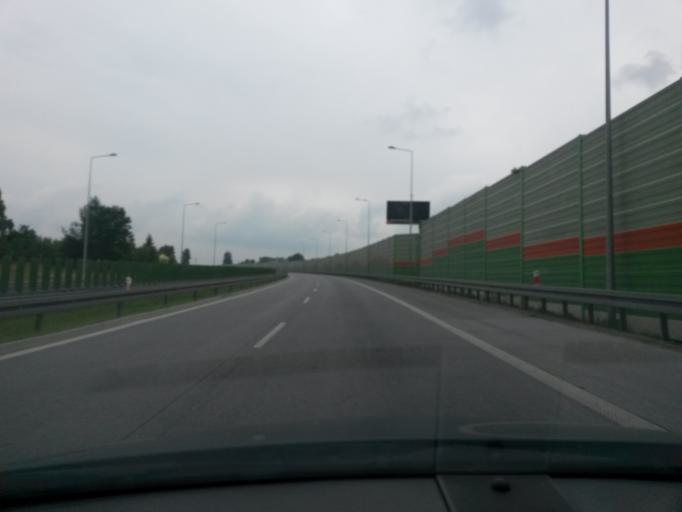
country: PL
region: Lodz Voivodeship
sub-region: Powiat rawski
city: Rawa Mazowiecka
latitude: 51.7464
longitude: 20.2396
